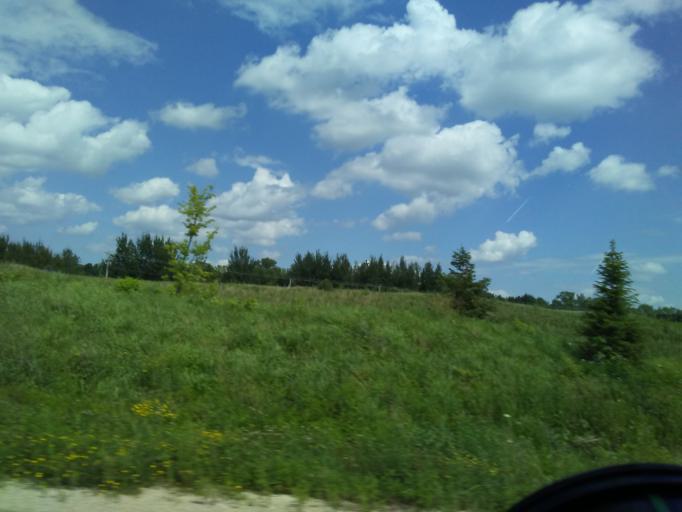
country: US
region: Wisconsin
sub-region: Dane County
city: Verona
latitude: 42.9999
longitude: -89.5581
